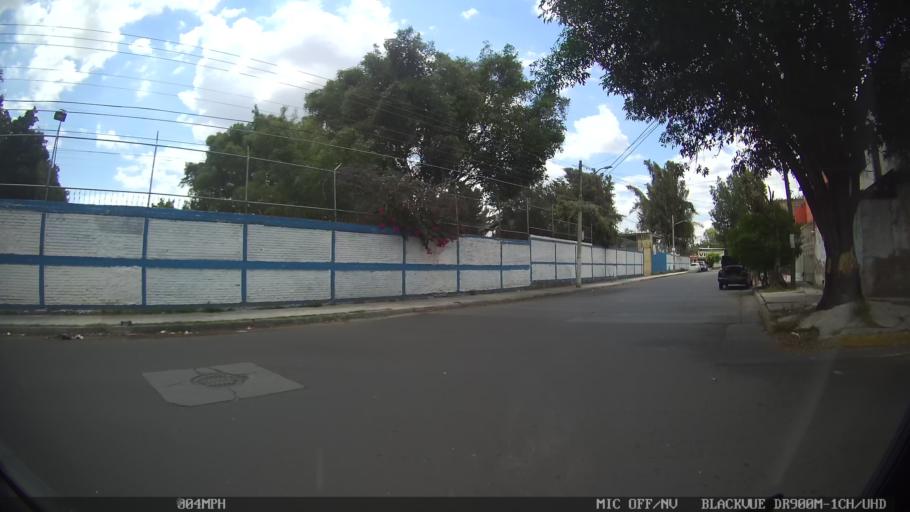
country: MX
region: Jalisco
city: Tlaquepaque
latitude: 20.6594
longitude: -103.2805
